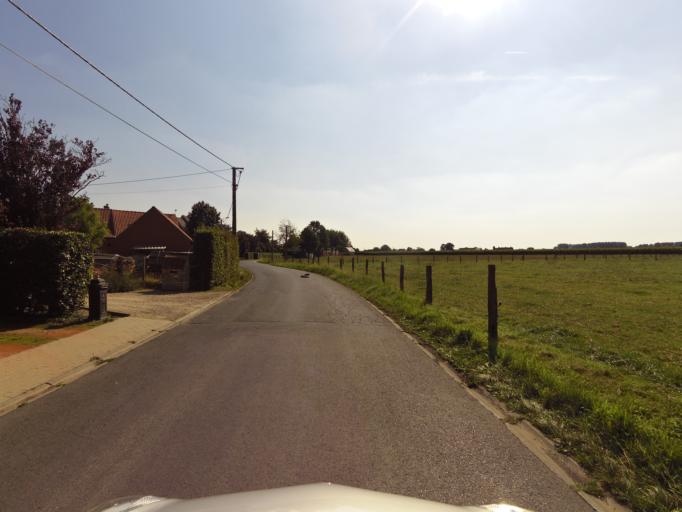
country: BE
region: Flanders
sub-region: Provincie West-Vlaanderen
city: Torhout
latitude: 51.0699
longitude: 3.0765
